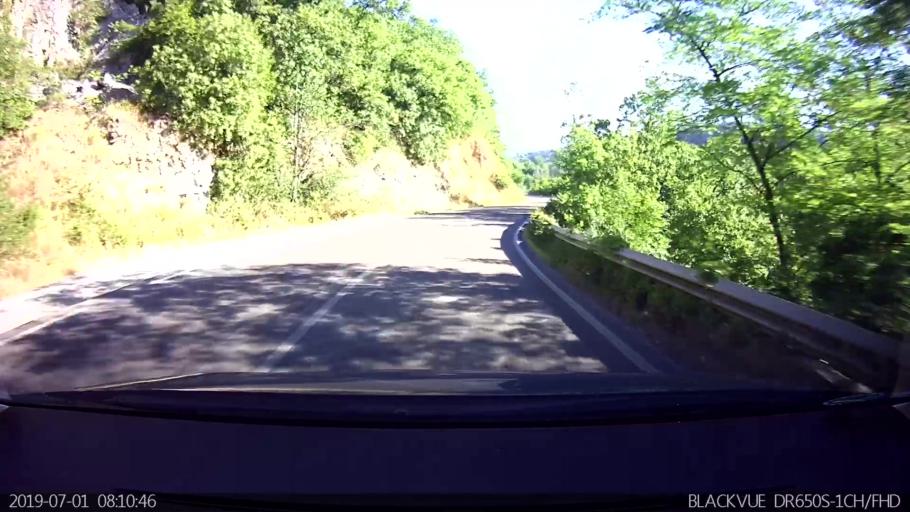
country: IT
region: Latium
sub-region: Provincia di Frosinone
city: Sant'Angelo in Villa-Giglio
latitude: 41.6722
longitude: 13.4215
